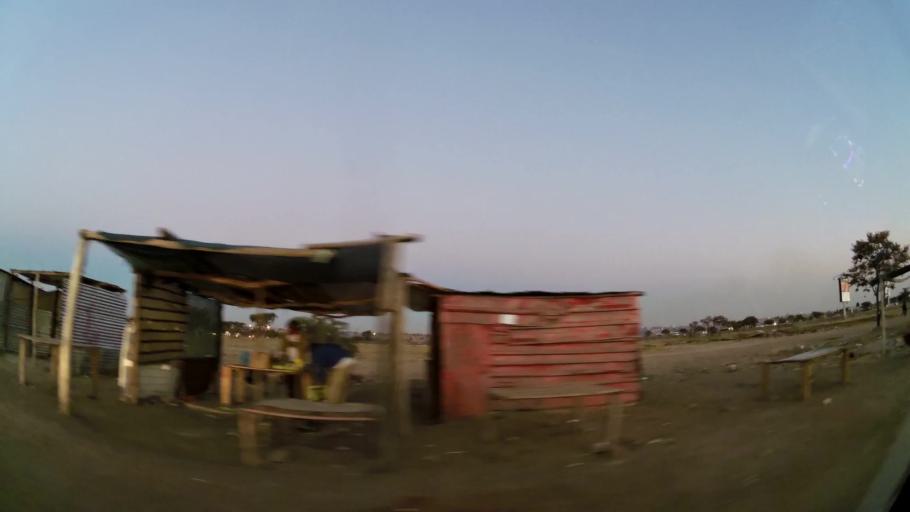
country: ZA
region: Limpopo
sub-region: Capricorn District Municipality
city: Polokwane
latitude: -23.8531
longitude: 29.3996
